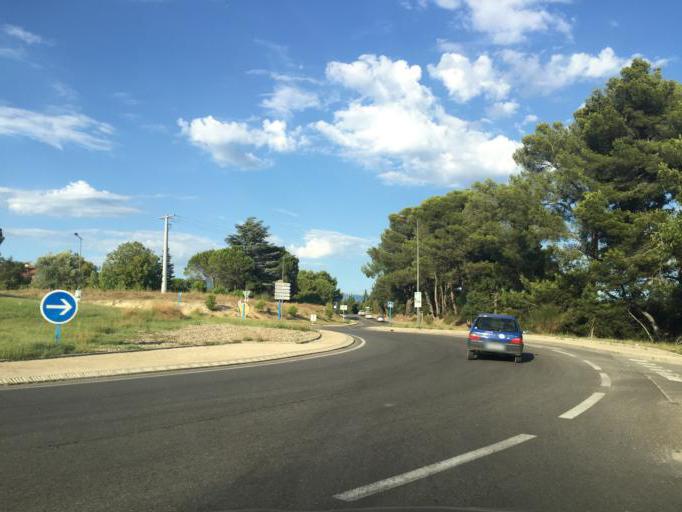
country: FR
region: Provence-Alpes-Cote d'Azur
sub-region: Departement du Vaucluse
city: Carpentras
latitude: 44.0666
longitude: 5.0675
